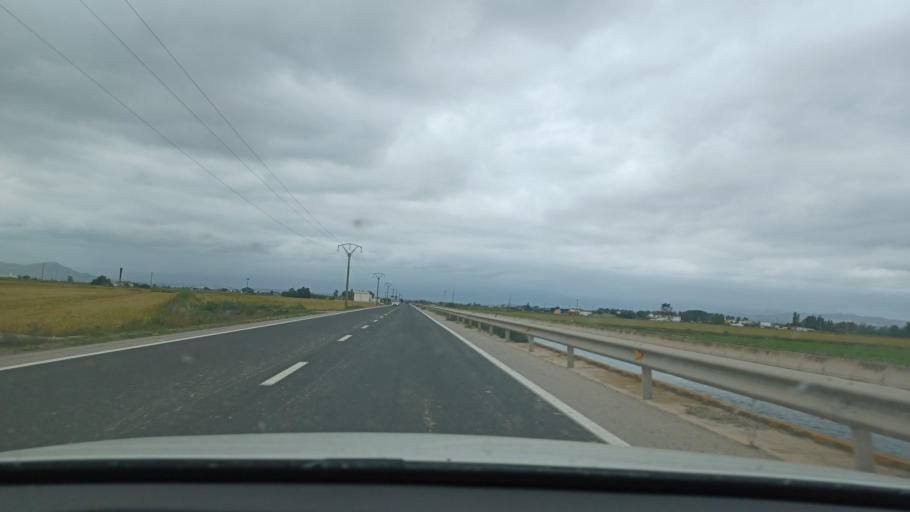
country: ES
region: Catalonia
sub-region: Provincia de Tarragona
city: Deltebre
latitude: 40.7087
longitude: 0.6901
